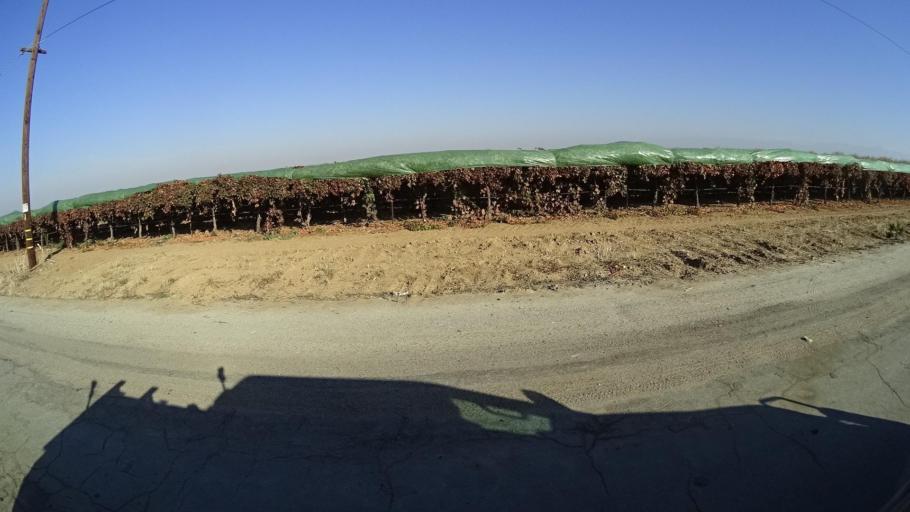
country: US
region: California
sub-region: Tulare County
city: Richgrove
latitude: 35.7323
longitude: -119.1146
